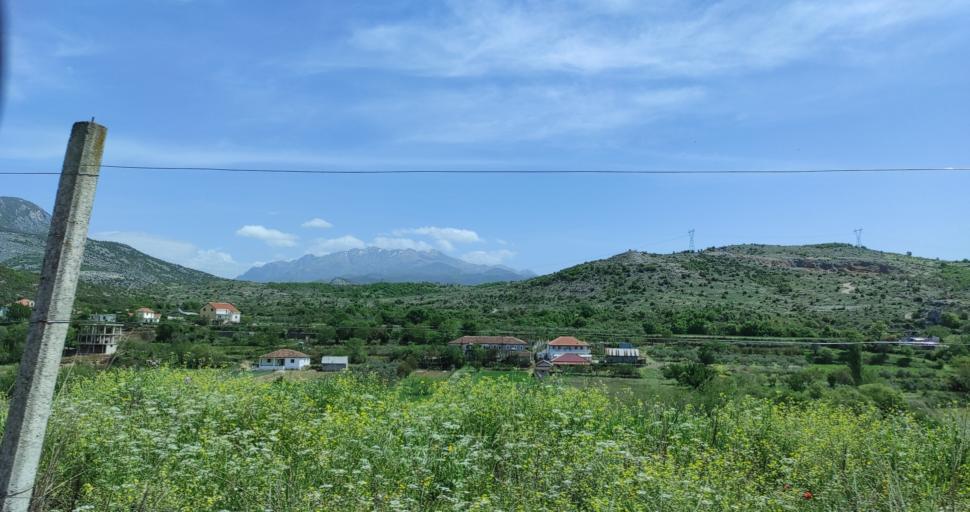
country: AL
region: Shkoder
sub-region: Rrethi i Malesia e Madhe
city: Gruemire
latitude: 42.1190
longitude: 19.5761
